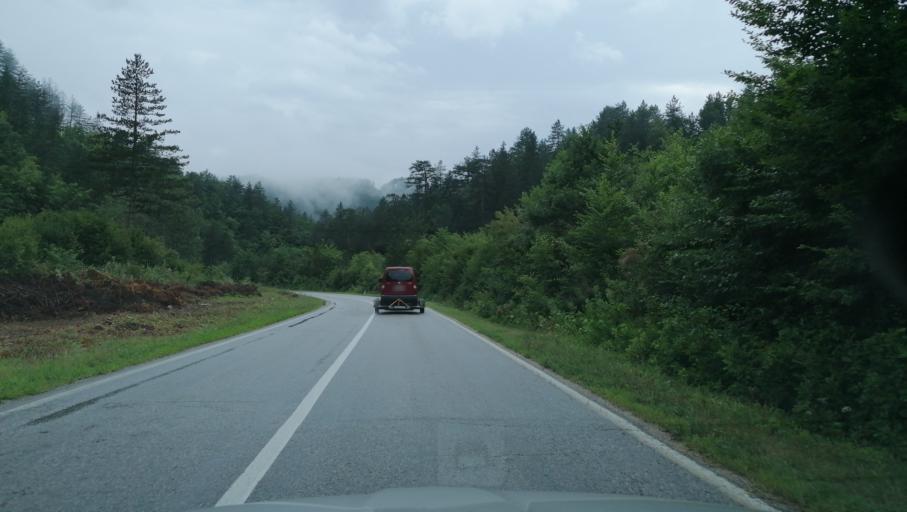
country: RS
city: Durici
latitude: 43.7774
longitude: 19.3755
